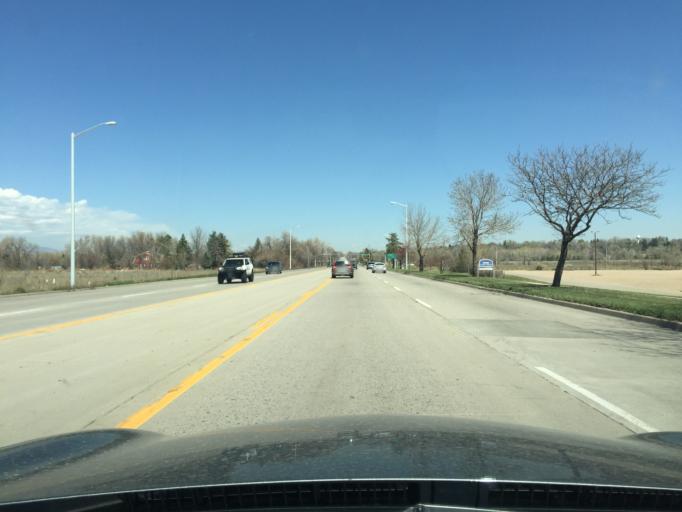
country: US
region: Colorado
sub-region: Boulder County
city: Longmont
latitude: 40.1568
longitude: -105.1306
